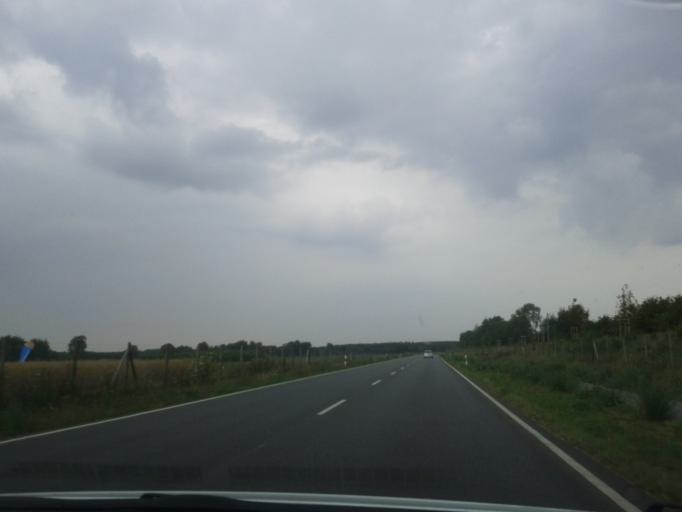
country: DE
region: Lower Saxony
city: Agathenburg
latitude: 53.5486
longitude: 9.4966
